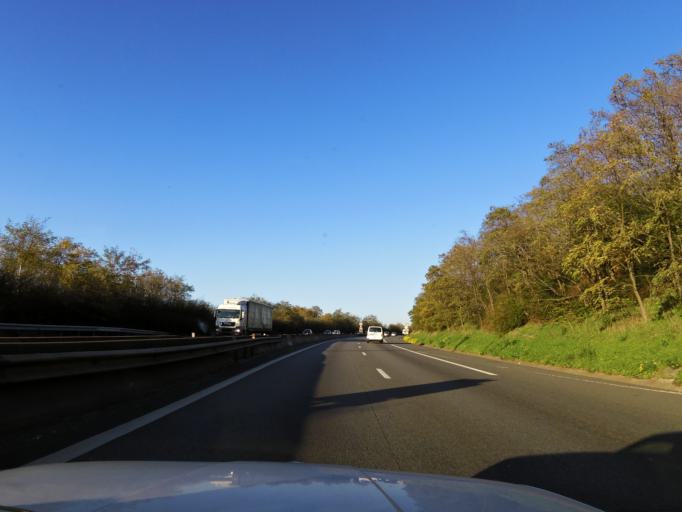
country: FR
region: Rhone-Alpes
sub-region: Departement du Rhone
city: Saint-Priest
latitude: 45.6872
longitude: 4.9627
